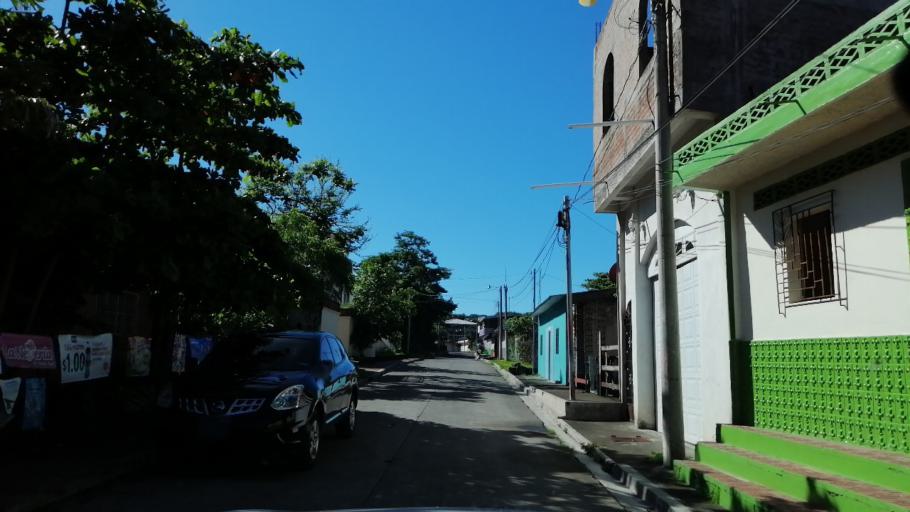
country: SV
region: Morazan
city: Corinto
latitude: 13.8100
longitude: -87.9734
